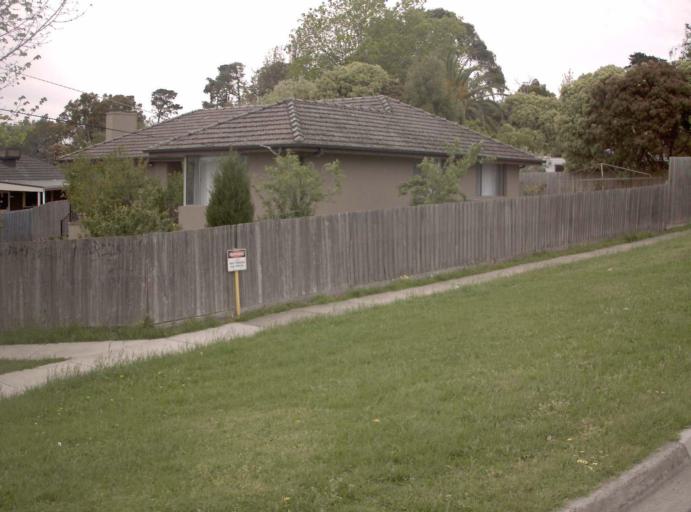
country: AU
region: Victoria
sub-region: Knox
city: Wantirna
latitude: -37.8426
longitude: 145.2274
